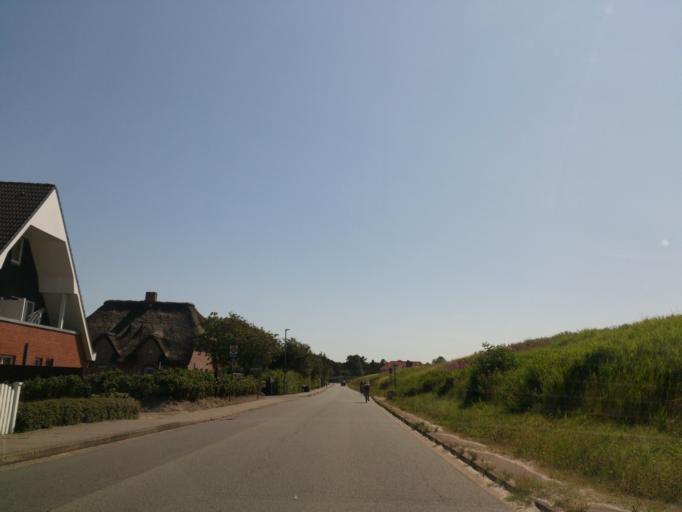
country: DE
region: Schleswig-Holstein
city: Sankt Peter-Ording
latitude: 54.3284
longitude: 8.6077
